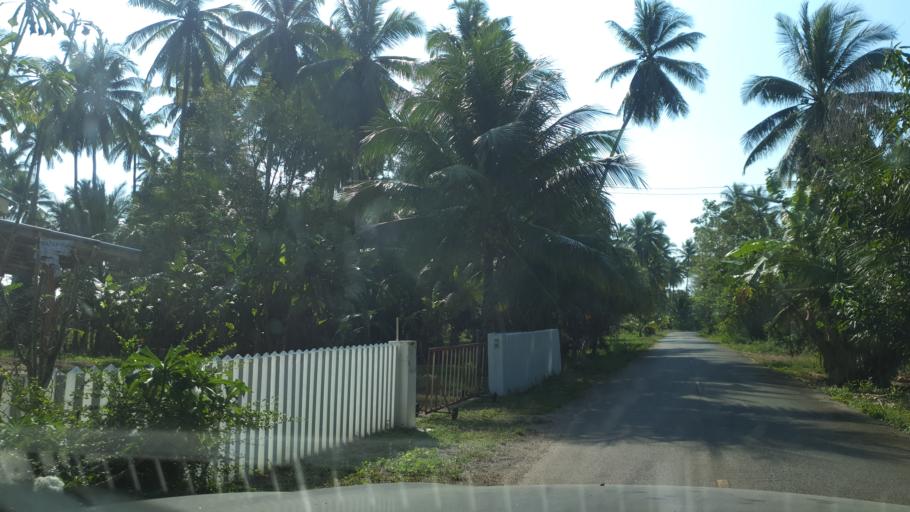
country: TH
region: Prachuap Khiri Khan
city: Thap Sakae
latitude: 11.3635
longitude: 99.5527
